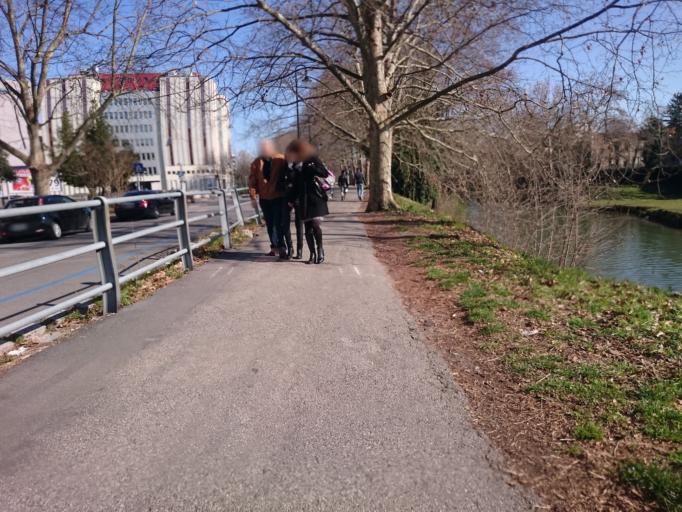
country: IT
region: Veneto
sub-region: Provincia di Padova
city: Padova
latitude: 45.4114
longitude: 11.8859
